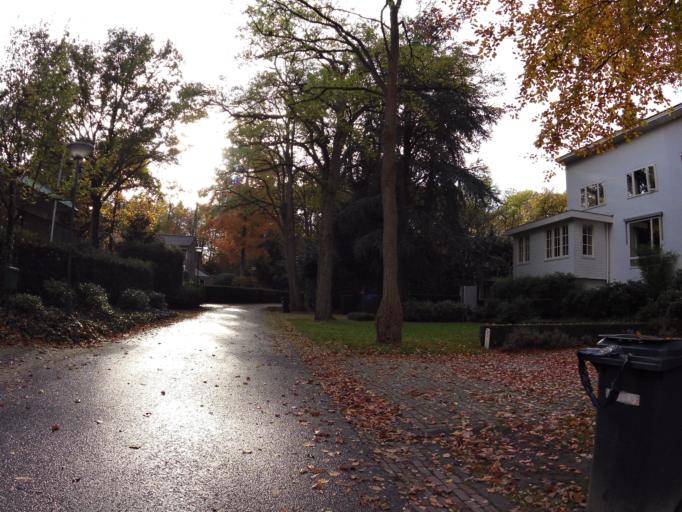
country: NL
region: North Brabant
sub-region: Gemeente Vught
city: Vught
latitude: 51.6538
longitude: 5.2790
